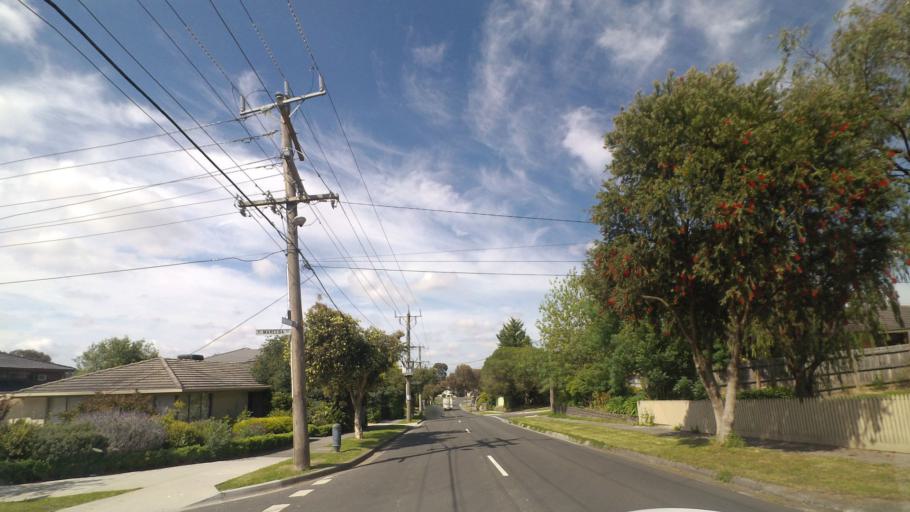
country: AU
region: Victoria
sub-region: Knox
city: Bayswater
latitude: -37.8539
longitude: 145.2525
